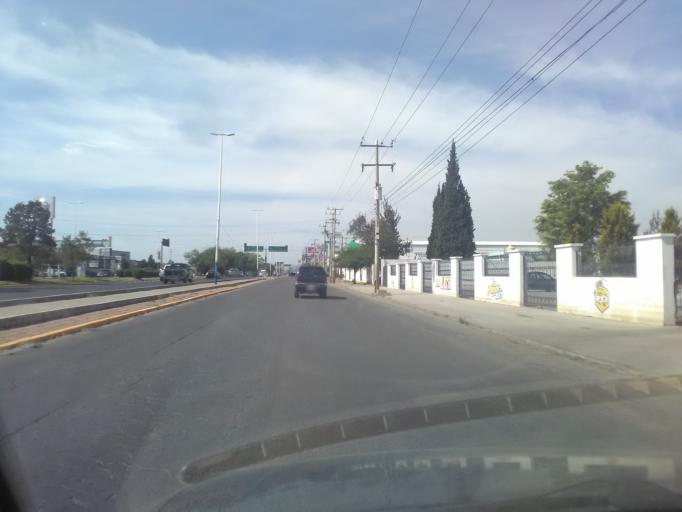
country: MX
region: Durango
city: Victoria de Durango
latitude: 24.0490
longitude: -104.6218
